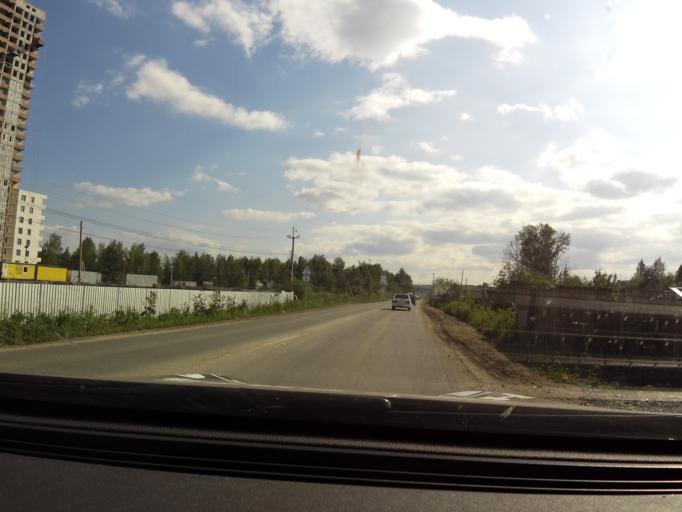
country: RU
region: Sverdlovsk
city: Shirokaya Rechka
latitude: 56.7962
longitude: 60.4907
